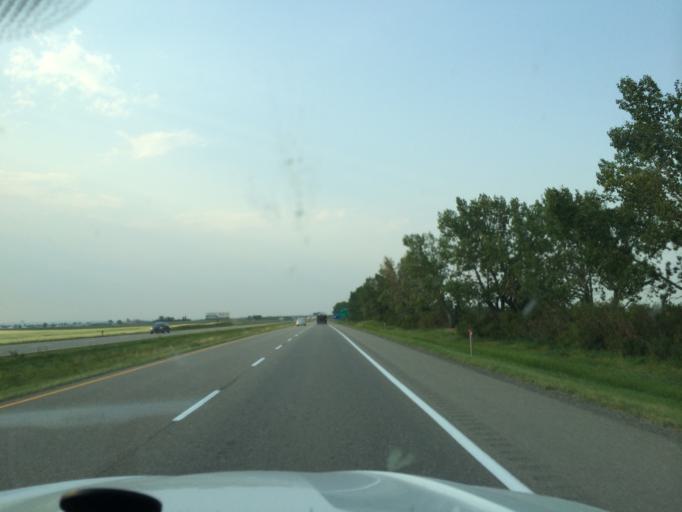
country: CA
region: Alberta
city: High River
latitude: 50.5613
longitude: -113.8280
